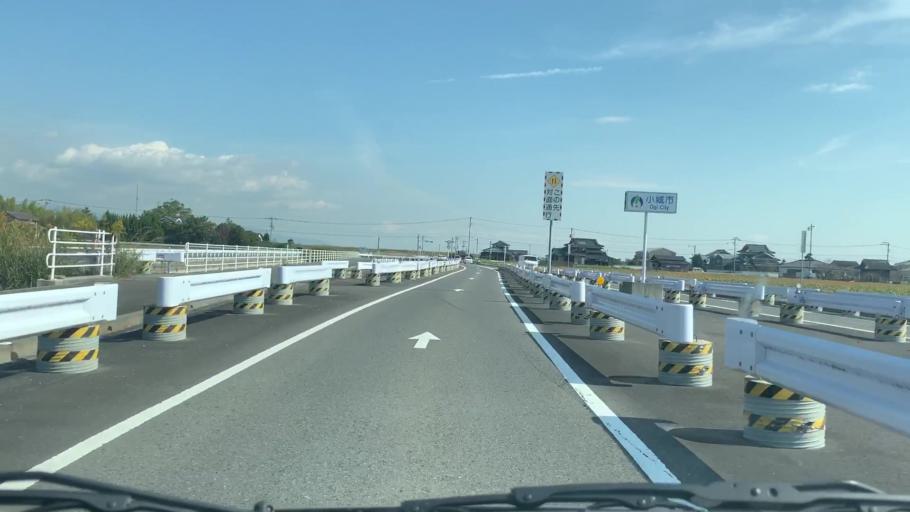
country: JP
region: Saga Prefecture
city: Saga-shi
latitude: 33.2224
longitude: 130.1826
